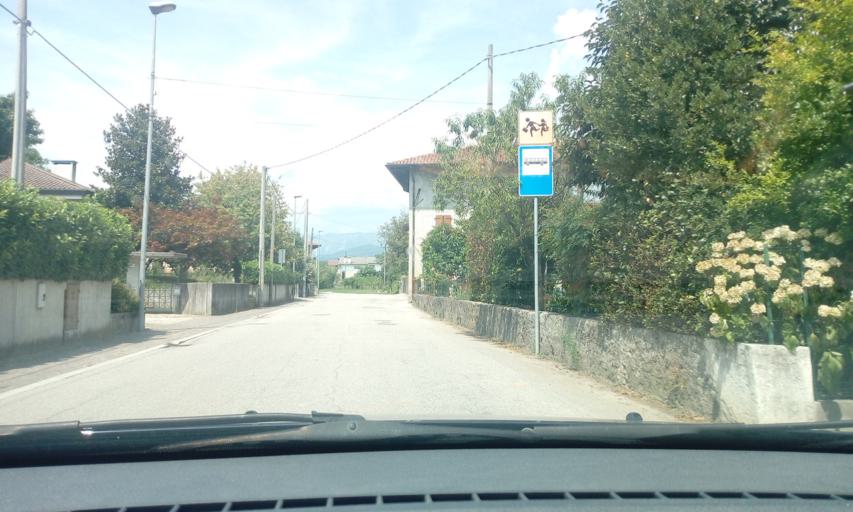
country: IT
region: Friuli Venezia Giulia
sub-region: Provincia di Udine
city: Faedis
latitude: 46.1373
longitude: 13.3182
